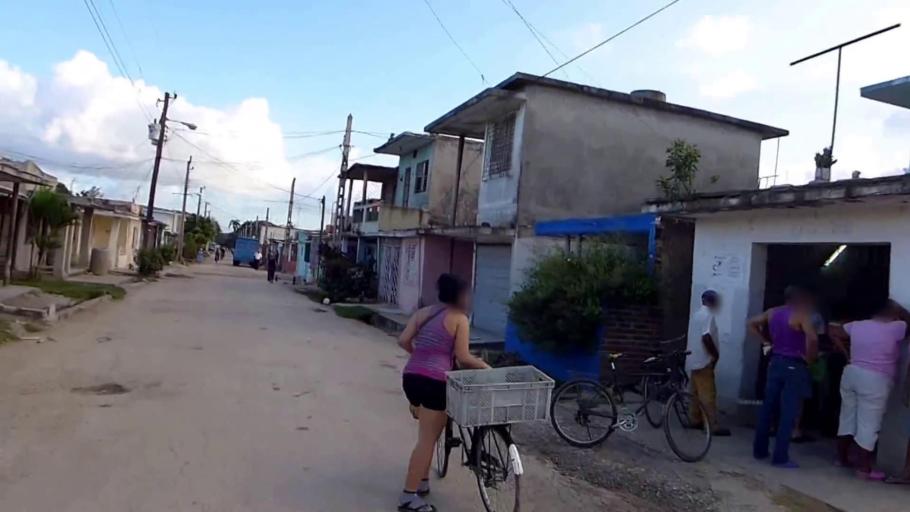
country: CU
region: Camaguey
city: Camaguey
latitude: 21.3981
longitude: -77.9054
